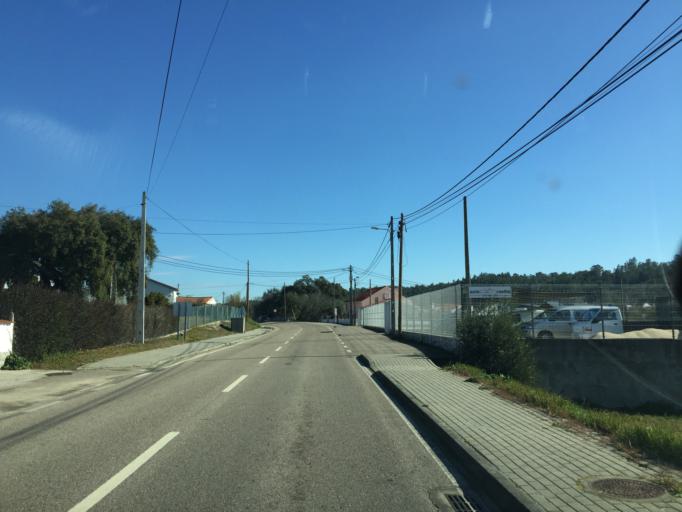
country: PT
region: Portalegre
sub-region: Ponte de Sor
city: Ponte de Sor
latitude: 39.3367
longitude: -7.9805
